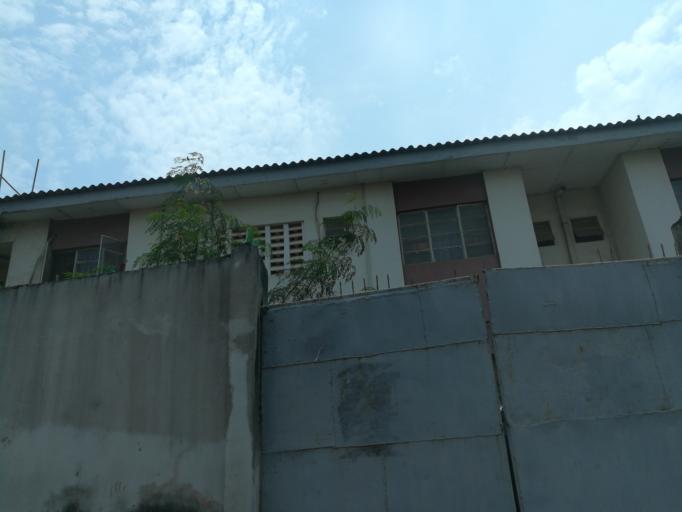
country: NG
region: Lagos
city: Oshodi
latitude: 6.5508
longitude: 3.3235
